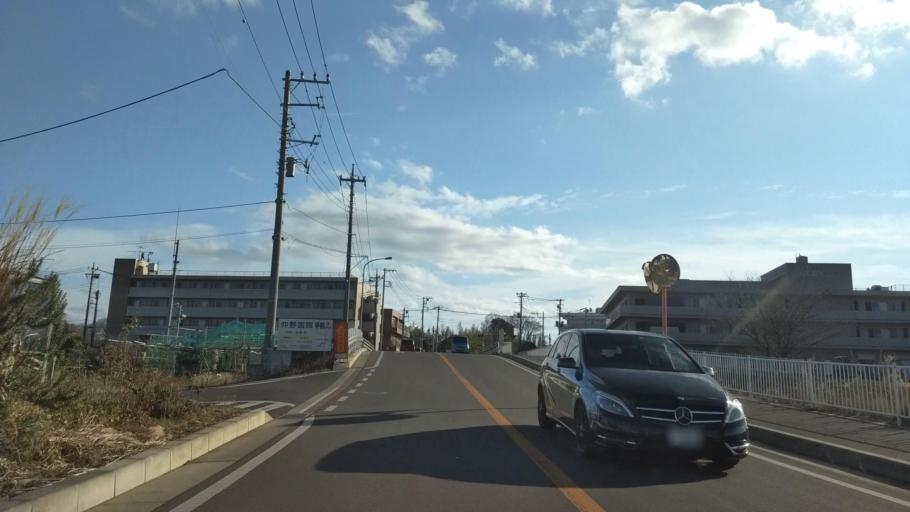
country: JP
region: Kanagawa
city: Isehara
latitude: 35.3738
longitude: 139.2837
